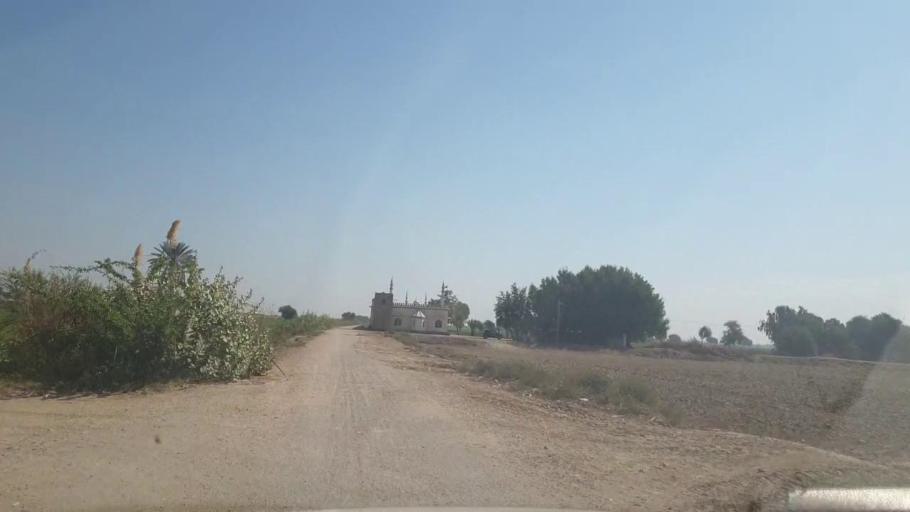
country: PK
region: Sindh
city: Mirpur Khas
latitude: 25.5396
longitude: 69.1904
